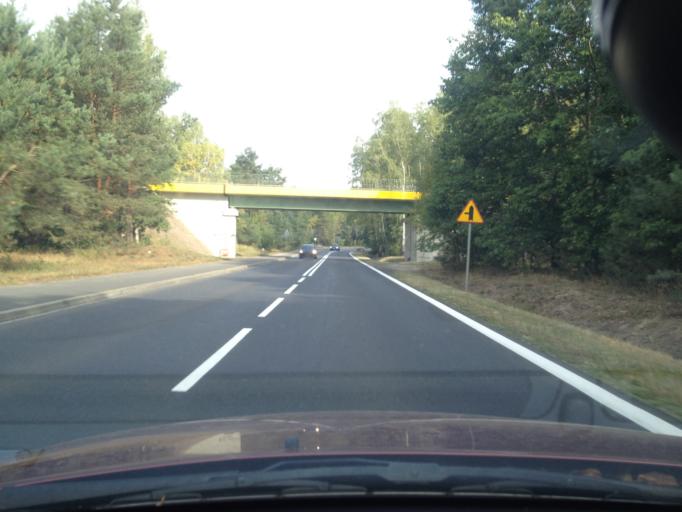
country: PL
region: Lubusz
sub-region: Powiat zaganski
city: Szprotawa
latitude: 51.4423
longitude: 15.6001
